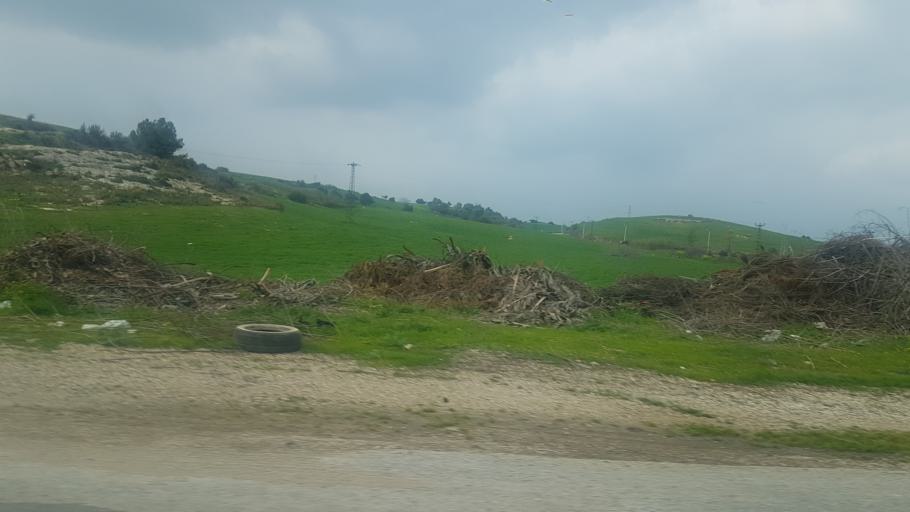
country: TR
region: Adana
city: Seyhan
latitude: 37.0563
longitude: 35.2242
